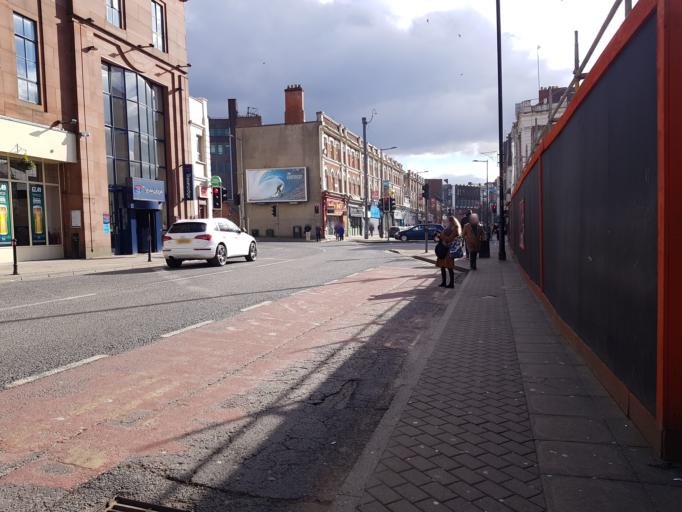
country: GB
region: Northern Ireland
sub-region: City of Derry
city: Derry
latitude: 54.9997
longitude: -7.3220
